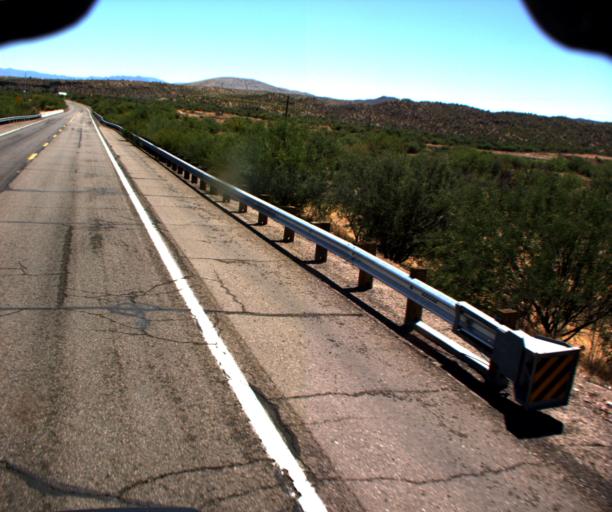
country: US
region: Arizona
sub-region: Pinal County
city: Mammoth
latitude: 32.7441
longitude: -110.6475
